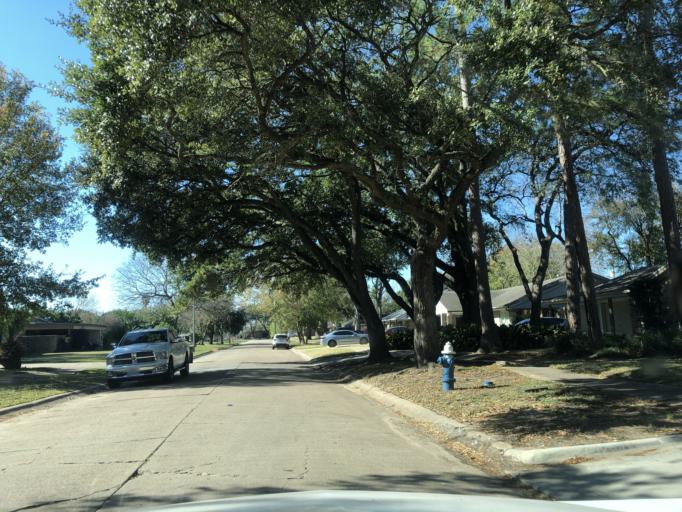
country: US
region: Texas
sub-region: Harris County
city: Bellaire
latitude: 29.6801
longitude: -95.5011
